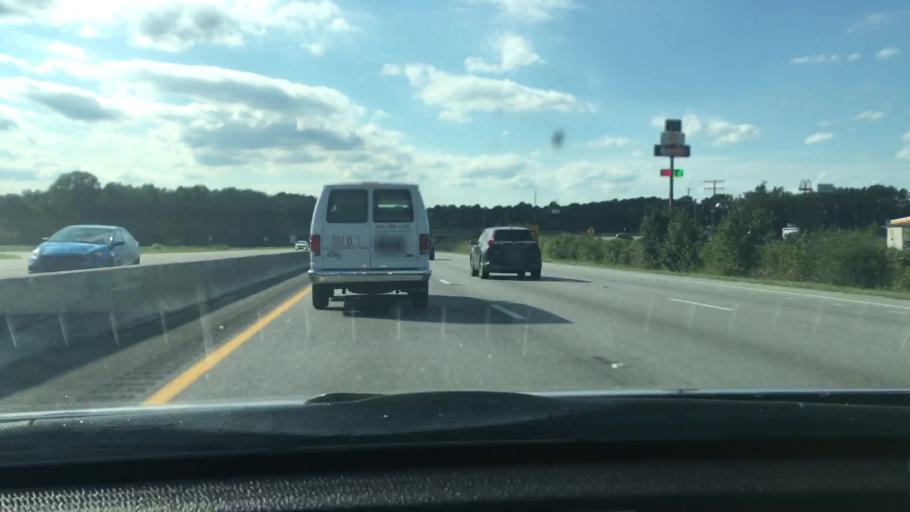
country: US
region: South Carolina
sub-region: Richland County
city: Dentsville
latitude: 34.0736
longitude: -80.9957
